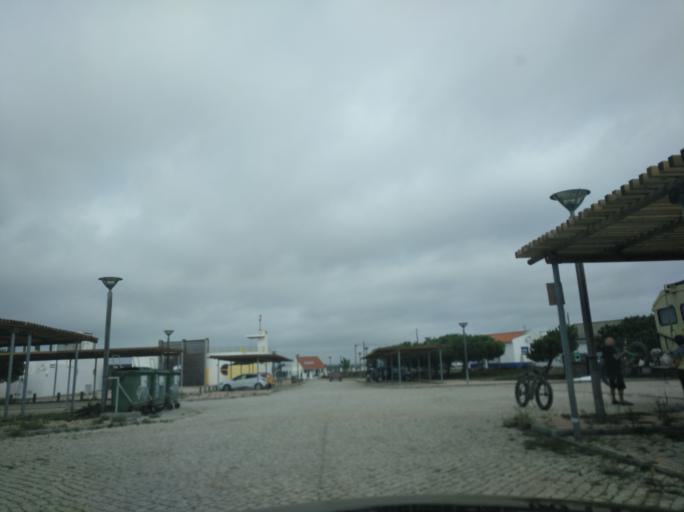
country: PT
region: Setubal
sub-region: Santiago do Cacem
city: Santo Andre
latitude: 38.1281
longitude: -8.7887
